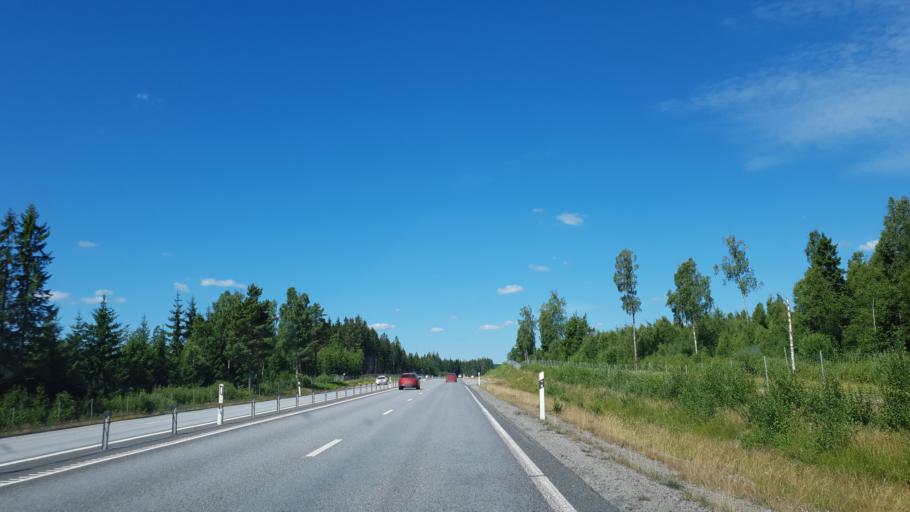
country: SE
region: Kronoberg
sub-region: Vaxjo Kommun
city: Gemla
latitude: 56.9081
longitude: 14.6482
